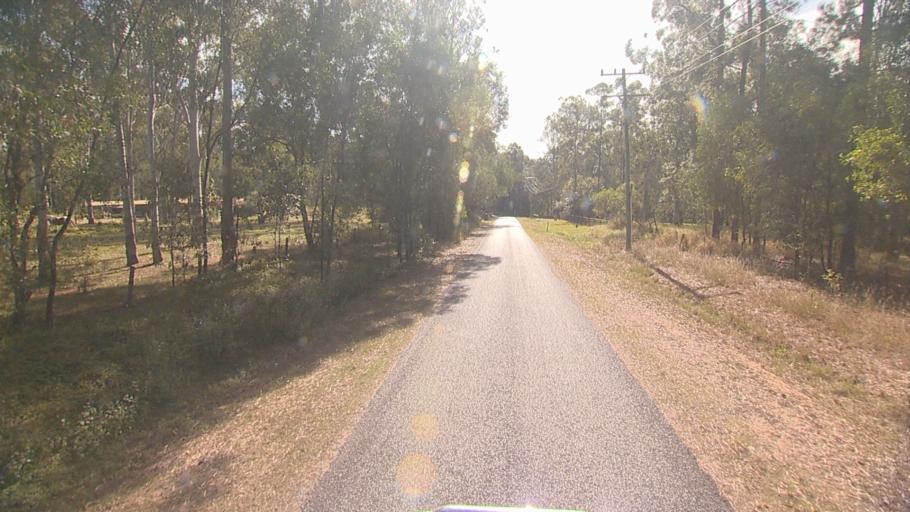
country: AU
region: Queensland
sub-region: Logan
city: North Maclean
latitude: -27.7815
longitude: 152.9935
